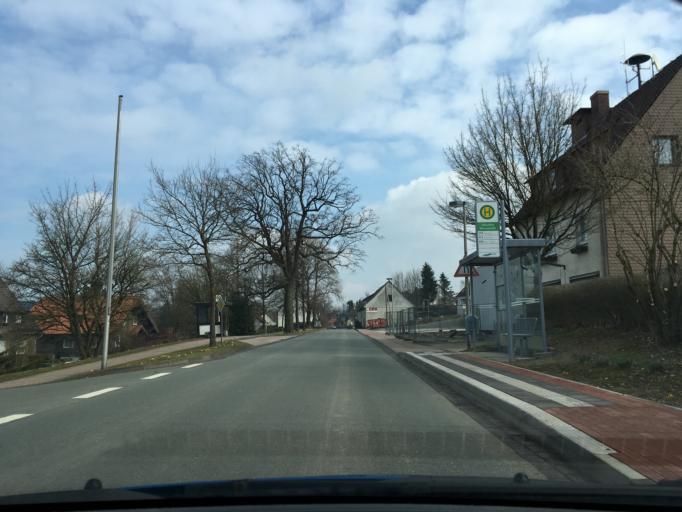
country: DE
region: Lower Saxony
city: Arholzen
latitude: 51.7644
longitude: 9.5422
